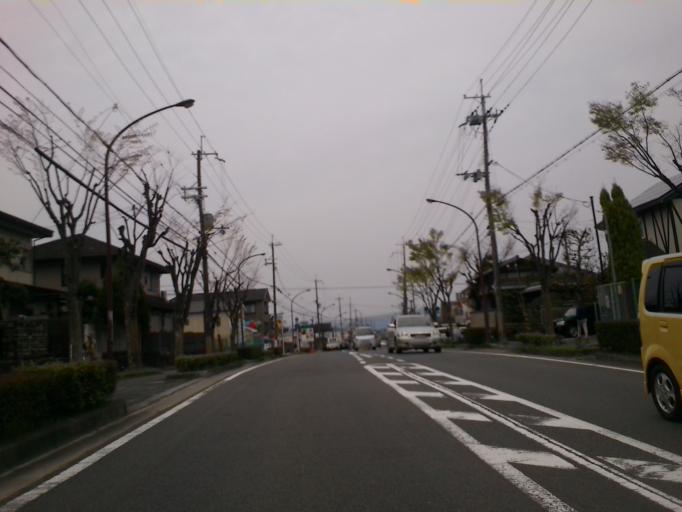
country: JP
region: Kyoto
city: Tanabe
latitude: 34.8301
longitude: 135.7328
